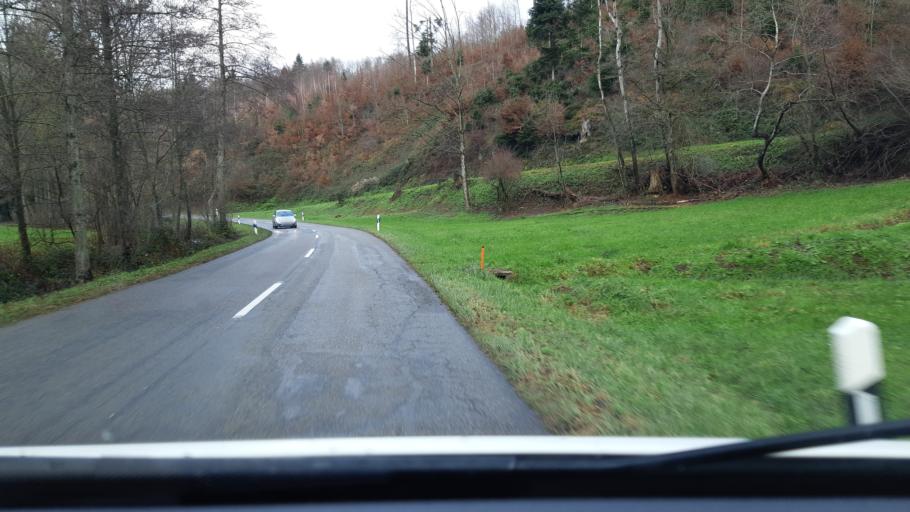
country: DE
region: Baden-Wuerttemberg
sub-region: Freiburg Region
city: Solden
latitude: 47.9183
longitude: 7.8091
